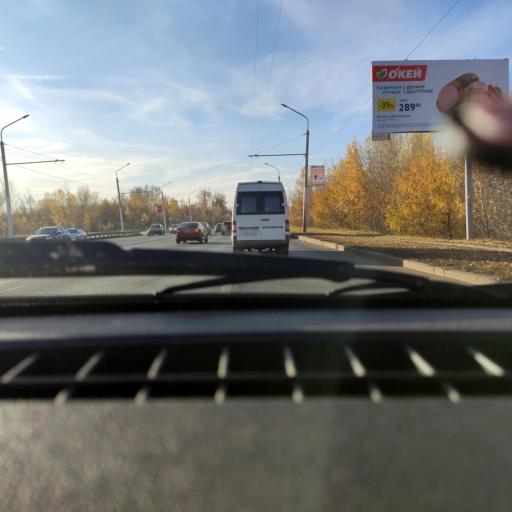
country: RU
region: Bashkortostan
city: Ufa
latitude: 54.7901
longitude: 56.0777
